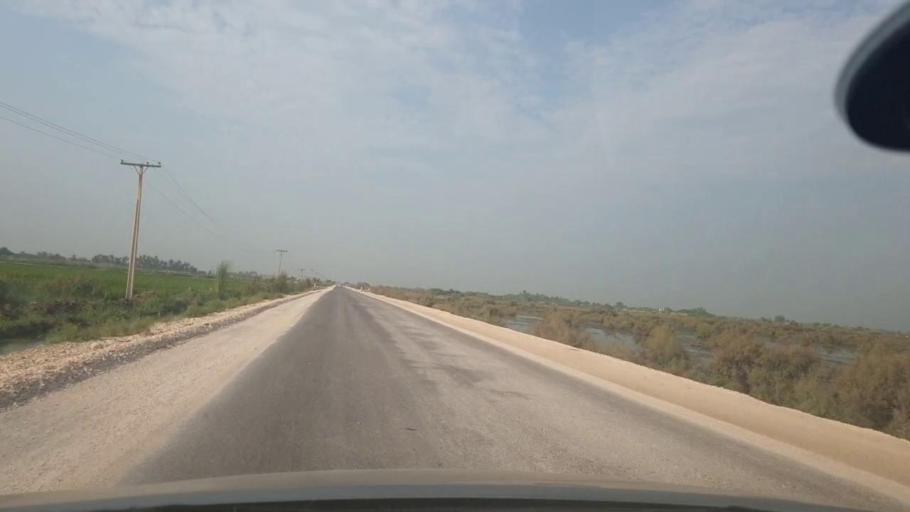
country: PK
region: Sindh
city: Jacobabad
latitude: 28.1448
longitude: 68.3455
